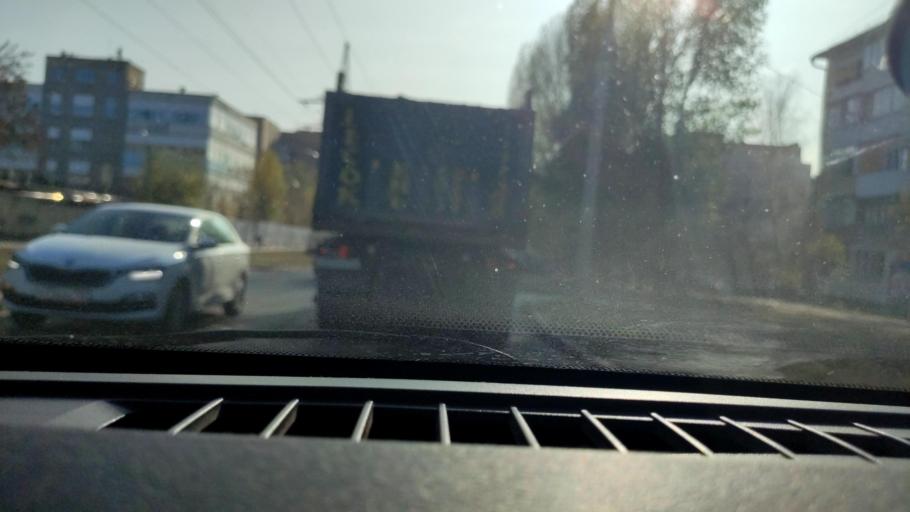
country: RU
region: Samara
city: Samara
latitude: 53.1926
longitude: 50.1719
